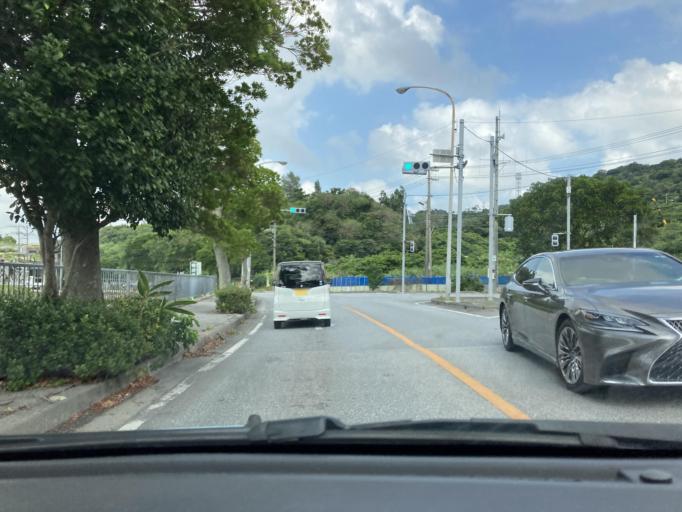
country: JP
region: Okinawa
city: Ginowan
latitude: 26.2726
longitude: 127.7806
